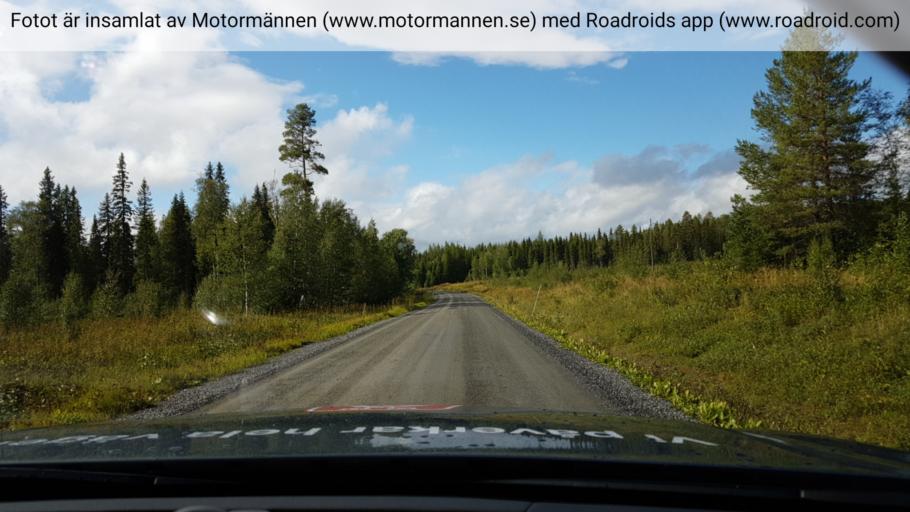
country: SE
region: Jaemtland
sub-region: Krokoms Kommun
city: Krokom
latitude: 63.7019
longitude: 14.5508
